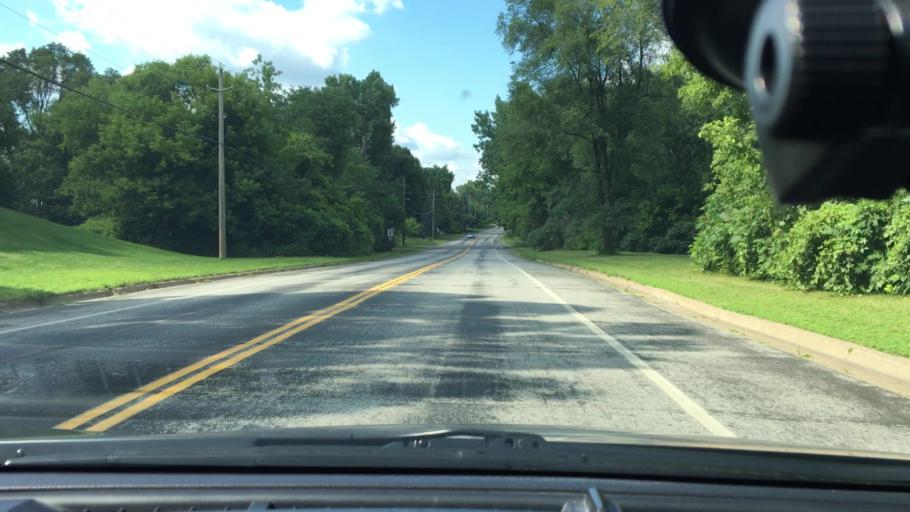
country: US
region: Minnesota
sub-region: Hennepin County
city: Plymouth
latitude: 45.0355
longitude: -93.4360
